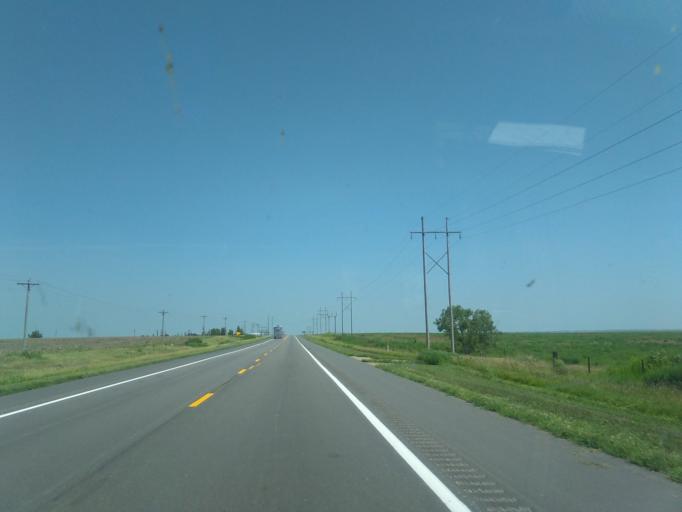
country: US
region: Nebraska
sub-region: Red Willow County
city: McCook
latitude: 40.2763
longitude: -100.6500
